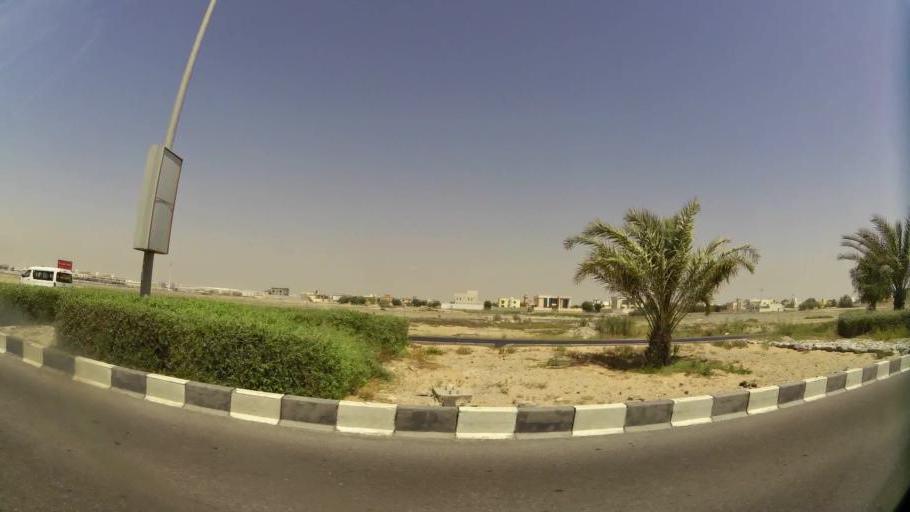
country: AE
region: Ajman
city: Ajman
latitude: 25.4311
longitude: 55.5030
